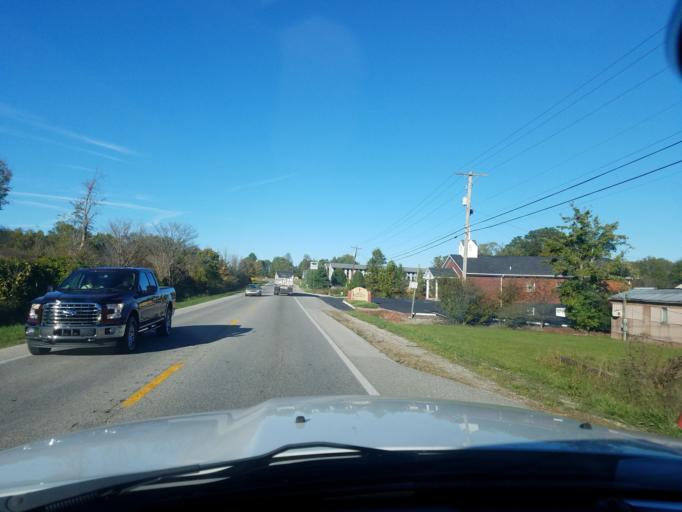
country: US
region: Kentucky
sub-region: Laurel County
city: London
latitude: 37.0443
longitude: -84.0541
